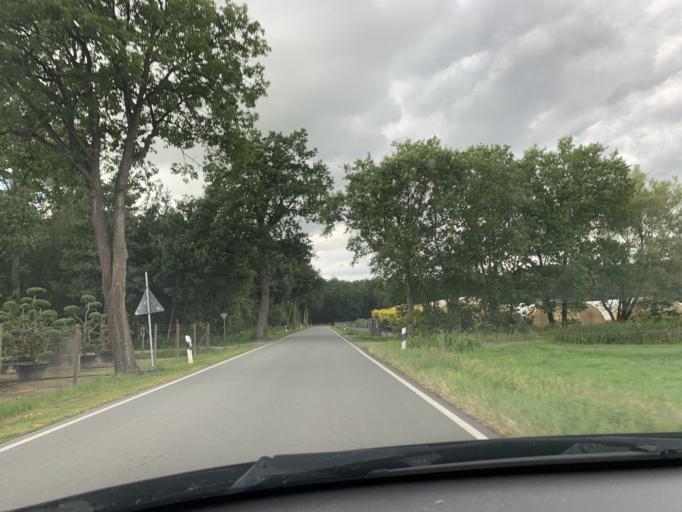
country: DE
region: Lower Saxony
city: Westerstede
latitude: 53.2137
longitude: 7.9252
